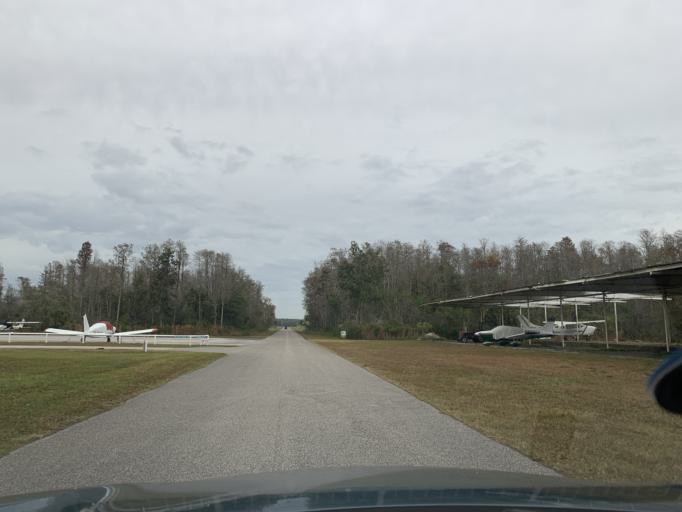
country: US
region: Florida
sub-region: Pasco County
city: Shady Hills
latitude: 28.3248
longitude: -82.4946
